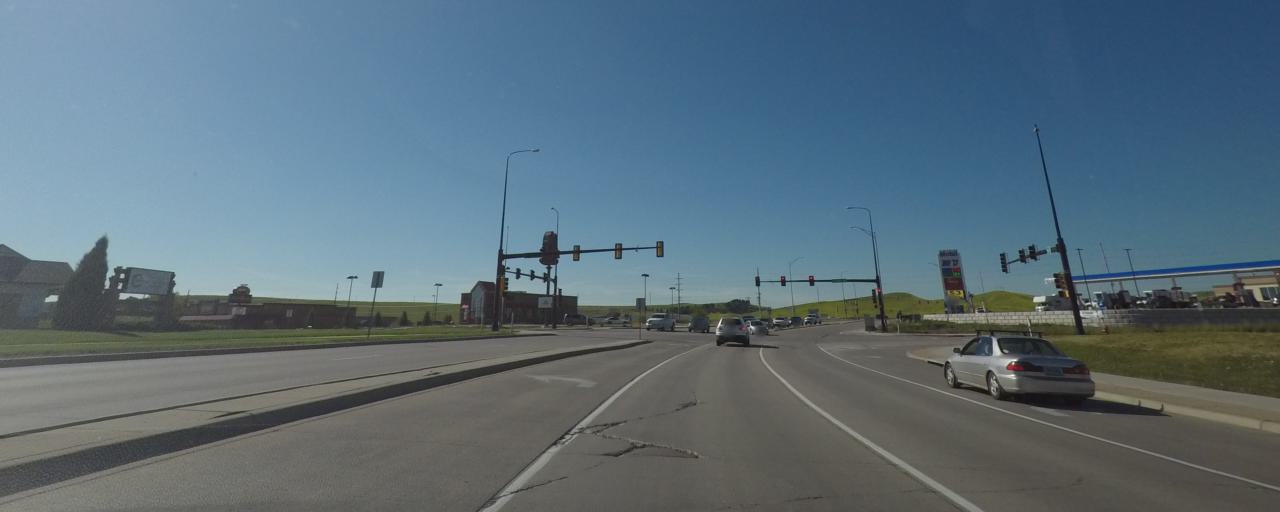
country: US
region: South Dakota
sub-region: Pennington County
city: Rapid City
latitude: 44.0336
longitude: -103.2123
